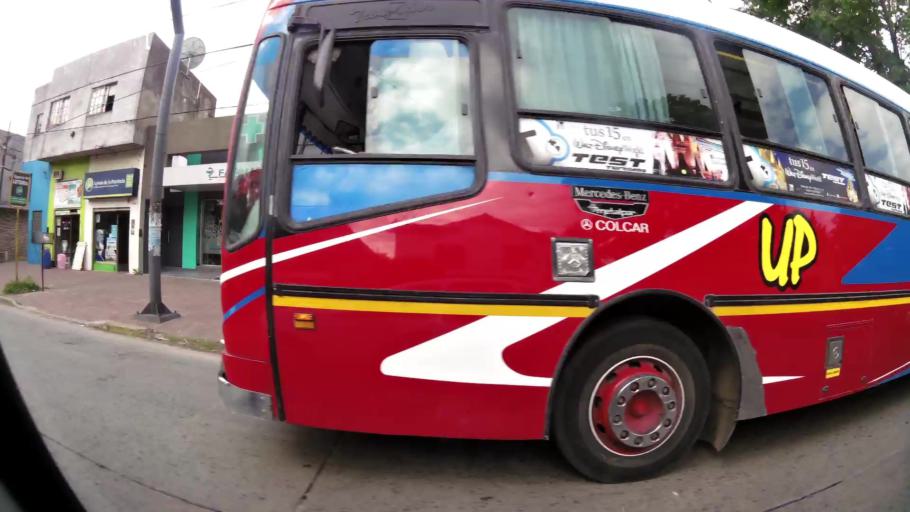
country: AR
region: Buenos Aires
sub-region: Partido de La Plata
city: La Plata
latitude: -34.9088
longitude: -57.9248
